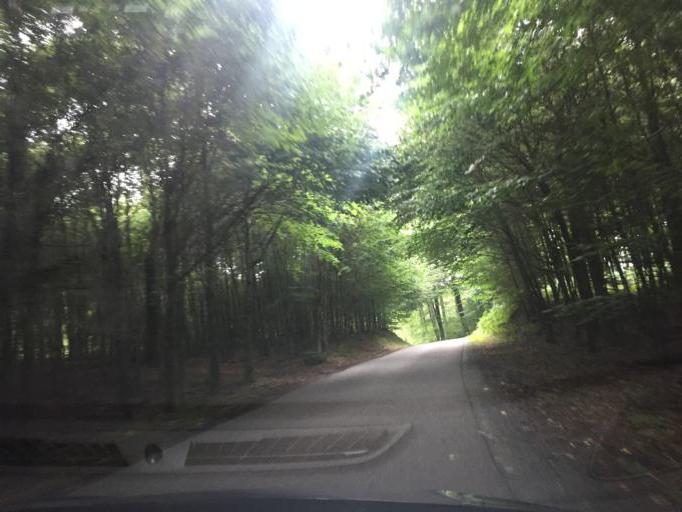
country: DK
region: South Denmark
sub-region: Assens Kommune
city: Tommerup Stationsby
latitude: 55.3721
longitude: 10.2204
